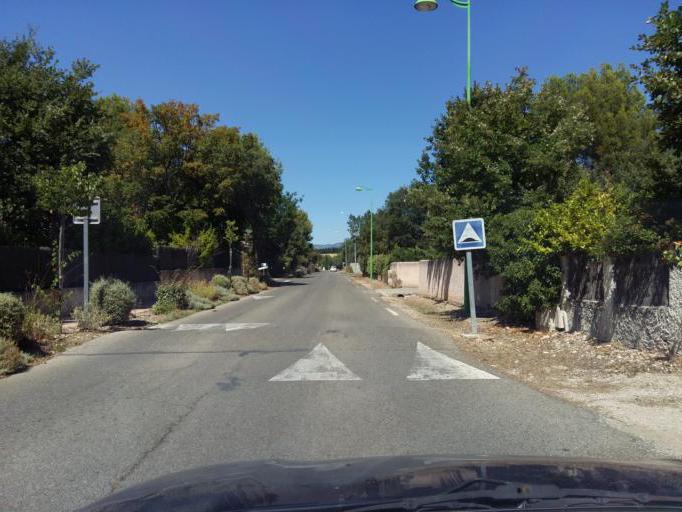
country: FR
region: Provence-Alpes-Cote d'Azur
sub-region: Departement du Vaucluse
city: Saint-Didier
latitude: 44.0192
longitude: 5.1097
